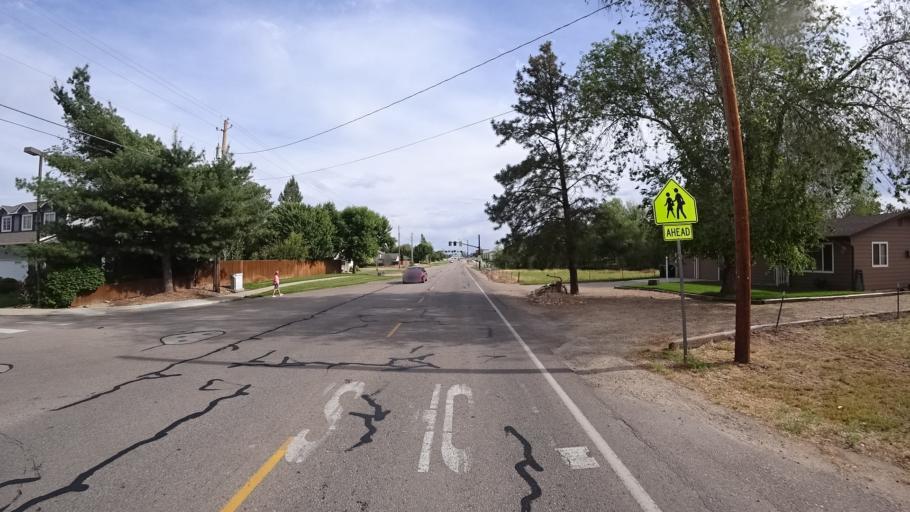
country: US
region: Idaho
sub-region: Ada County
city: Meridian
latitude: 43.5855
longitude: -116.3746
